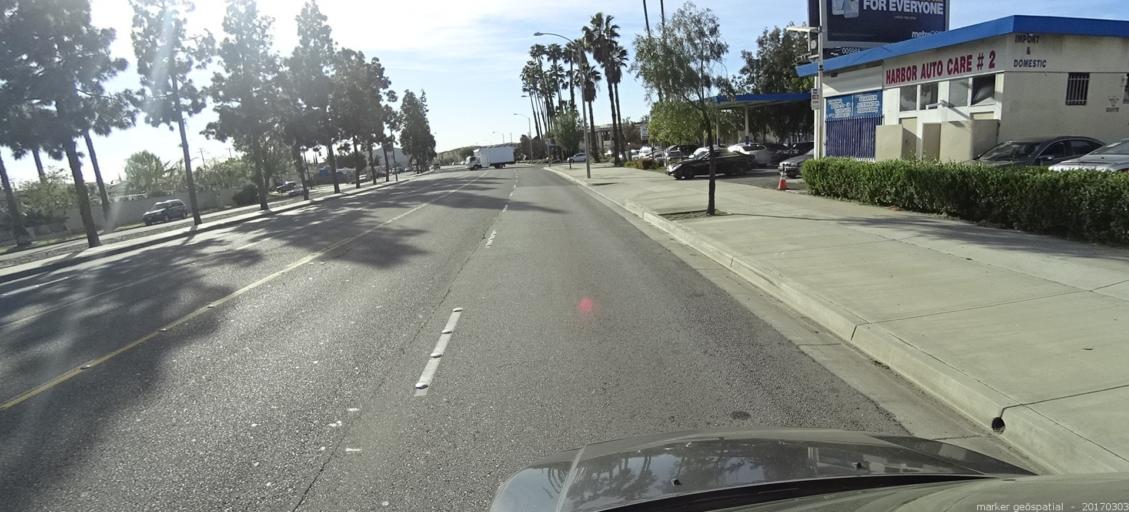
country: US
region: California
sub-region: Orange County
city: Anaheim
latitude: 33.8403
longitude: -117.8911
